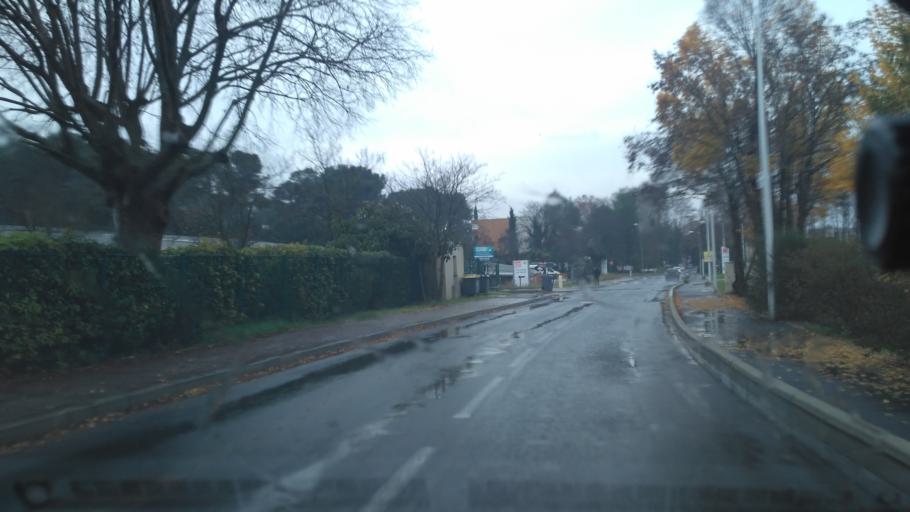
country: FR
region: Languedoc-Roussillon
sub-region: Departement de l'Herault
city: Clapiers
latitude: 43.6454
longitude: 3.8686
